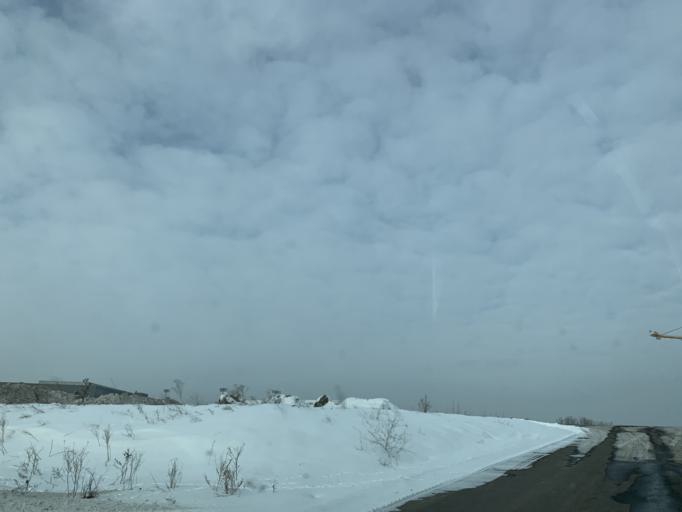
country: US
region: Minnesota
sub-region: Dakota County
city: Mendota Heights
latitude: 44.8568
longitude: -93.1132
